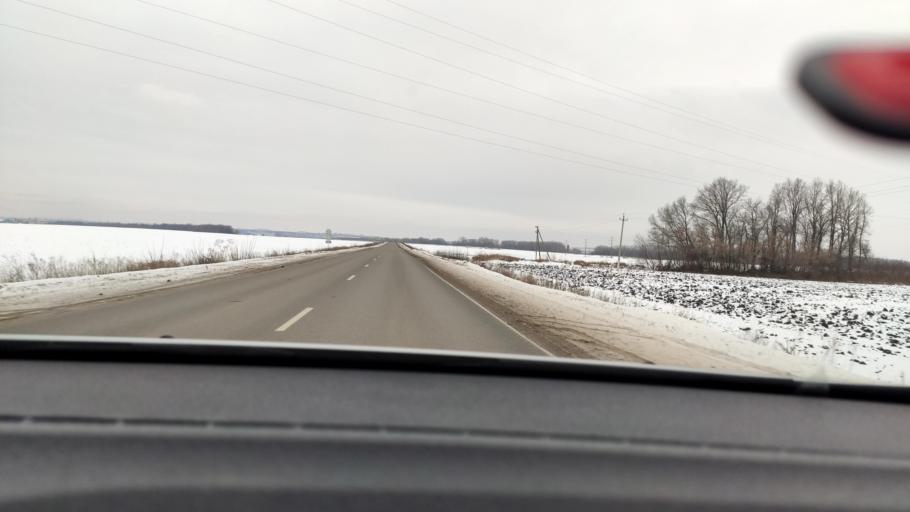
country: RU
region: Voronezj
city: Latnaya
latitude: 51.7424
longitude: 38.9396
